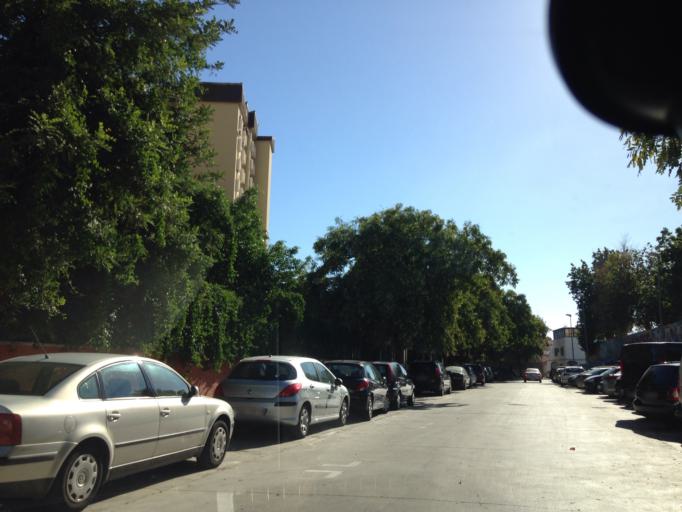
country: ES
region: Andalusia
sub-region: Provincia de Malaga
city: Malaga
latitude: 36.7204
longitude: -4.4410
